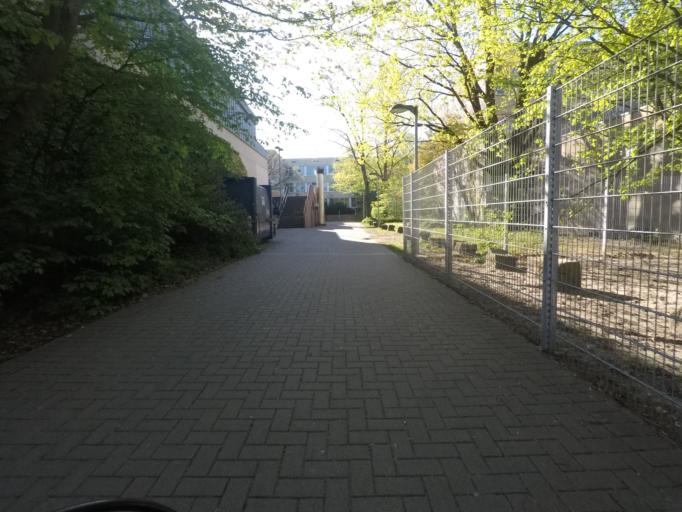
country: DE
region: North Rhine-Westphalia
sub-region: Regierungsbezirk Detmold
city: Bielefeld
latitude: 52.0297
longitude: 8.6011
